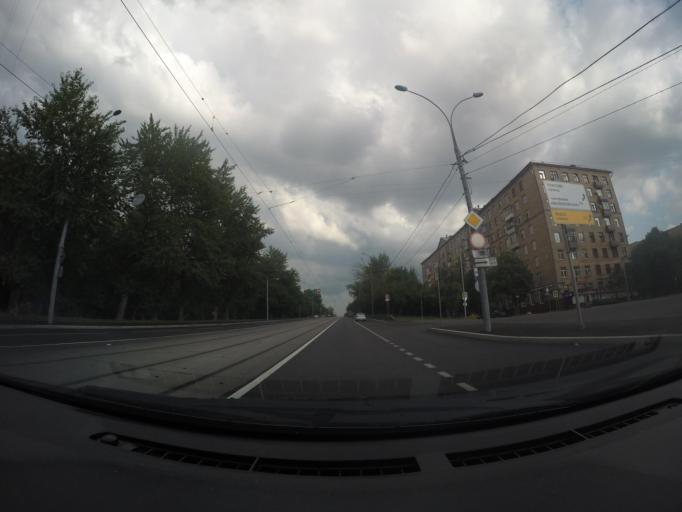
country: RU
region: Moscow
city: Rostokino
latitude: 55.8212
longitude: 37.6639
